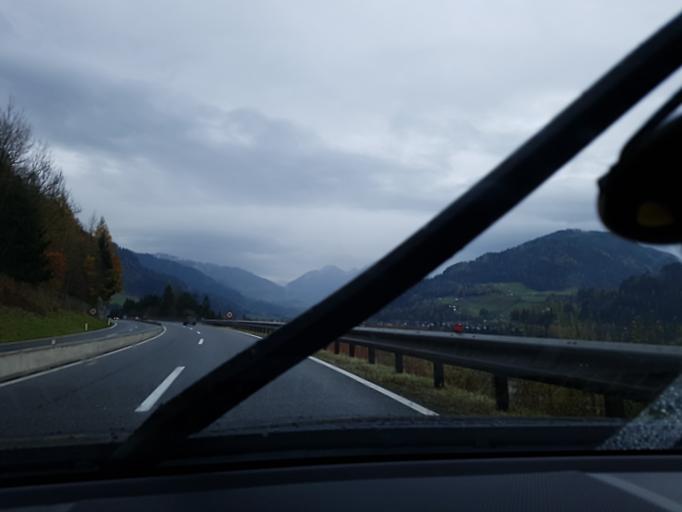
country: AT
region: Salzburg
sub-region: Politischer Bezirk Sankt Johann im Pongau
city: Bischofshofen
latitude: 47.4129
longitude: 13.2230
